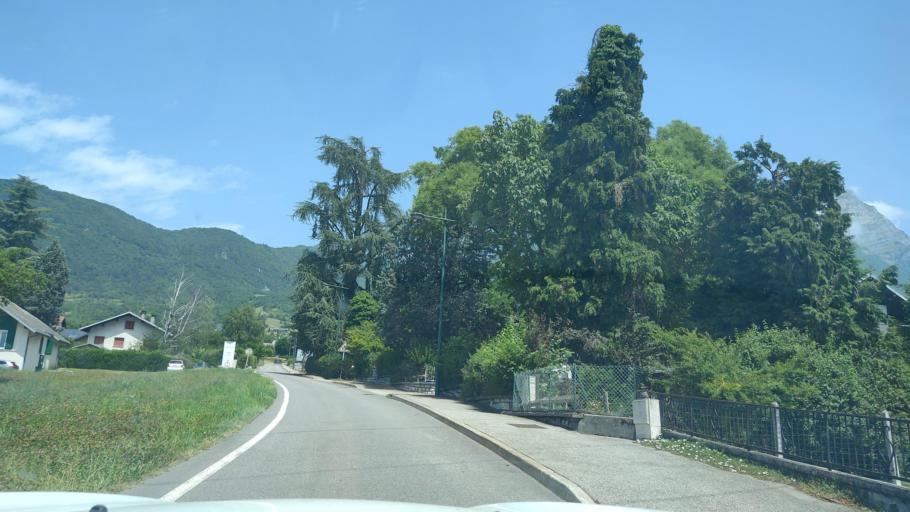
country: FR
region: Rhone-Alpes
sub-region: Departement de la Savoie
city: Coise-Saint-Jean-Pied-Gauthier
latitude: 45.5624
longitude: 6.1544
